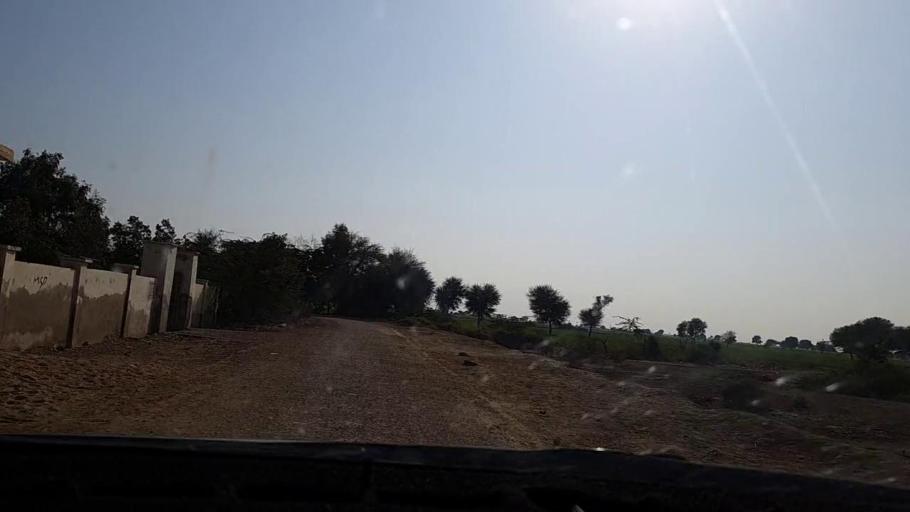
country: PK
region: Sindh
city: Tando Mittha Khan
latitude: 25.8261
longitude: 69.2800
